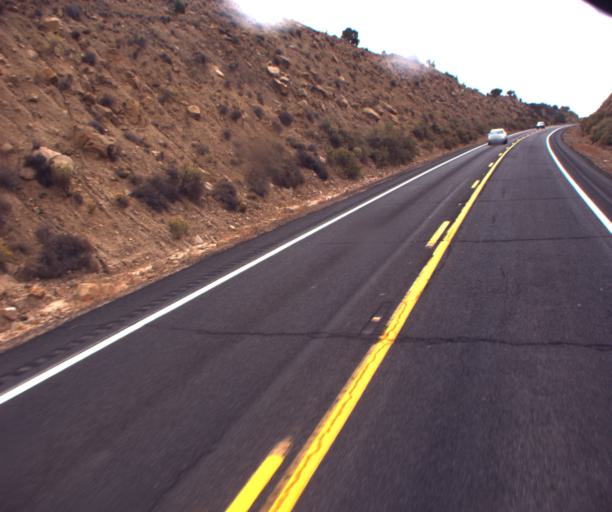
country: US
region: Arizona
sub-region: Navajo County
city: Kayenta
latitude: 36.6539
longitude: -110.4248
